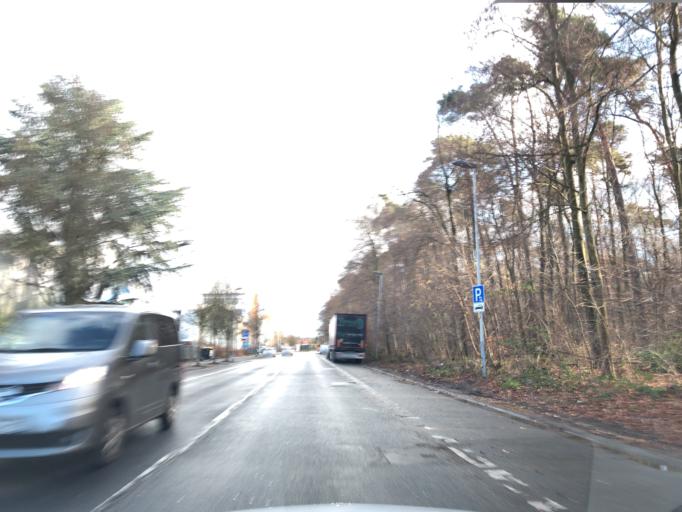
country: DE
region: Hesse
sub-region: Regierungsbezirk Darmstadt
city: Neu Isenburg
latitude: 50.0419
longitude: 8.6896
